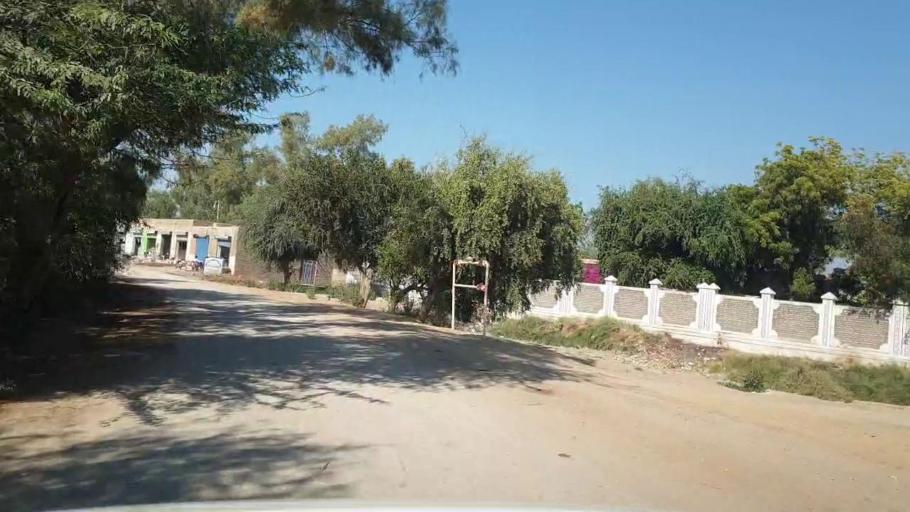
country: PK
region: Sindh
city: Bhan
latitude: 26.6490
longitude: 67.7139
